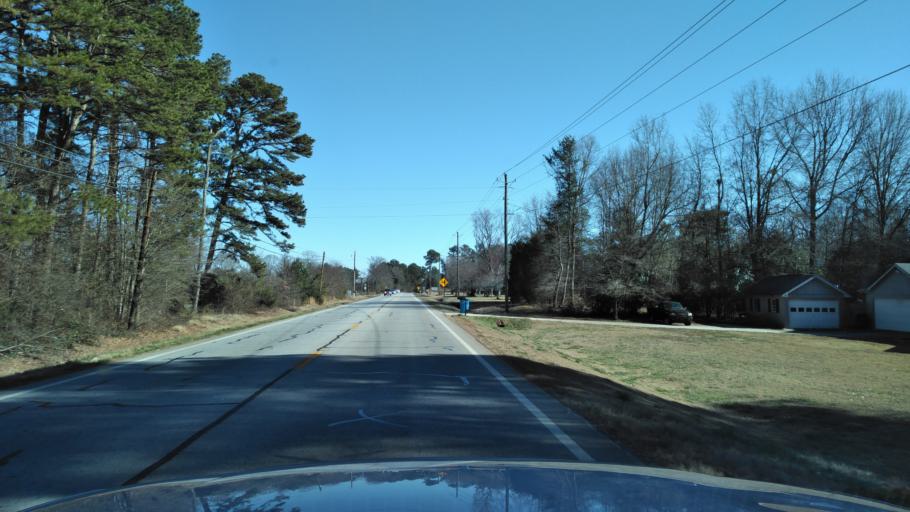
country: US
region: Georgia
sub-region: Jackson County
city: Commerce
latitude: 34.2347
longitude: -83.5057
